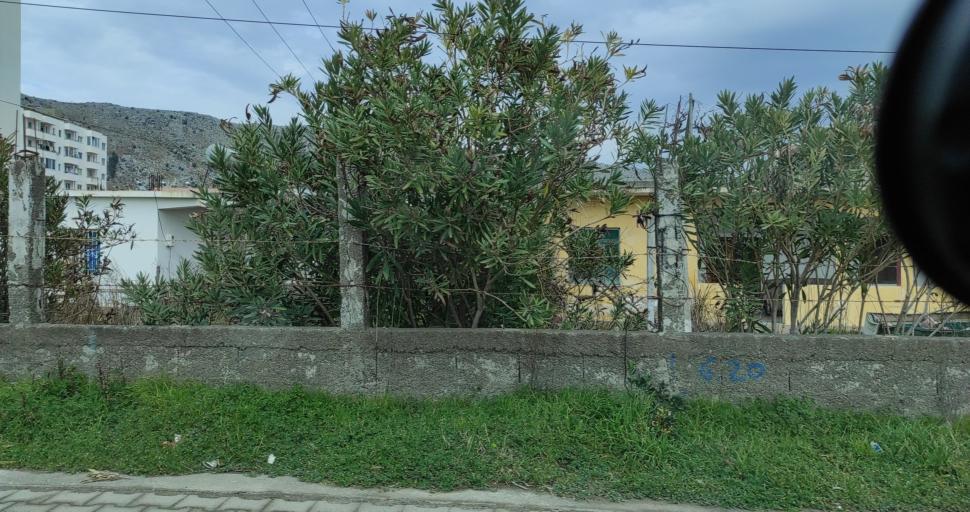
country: AL
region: Lezhe
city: Shengjin
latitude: 41.8024
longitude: 19.6008
